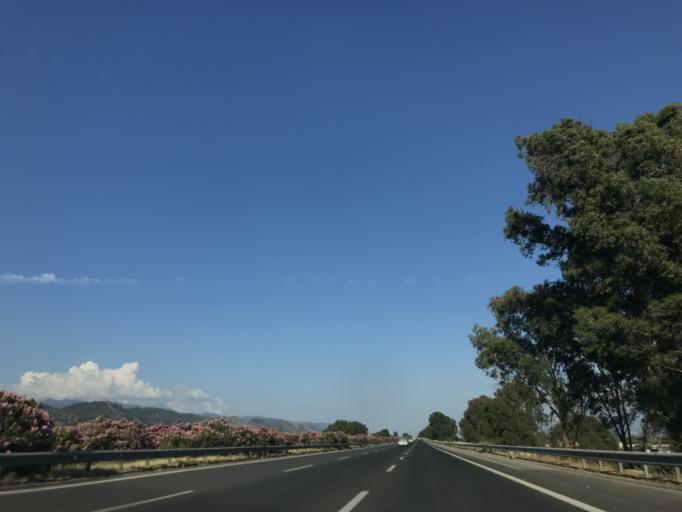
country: TR
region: Aydin
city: Germencik
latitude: 37.8701
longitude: 27.6414
